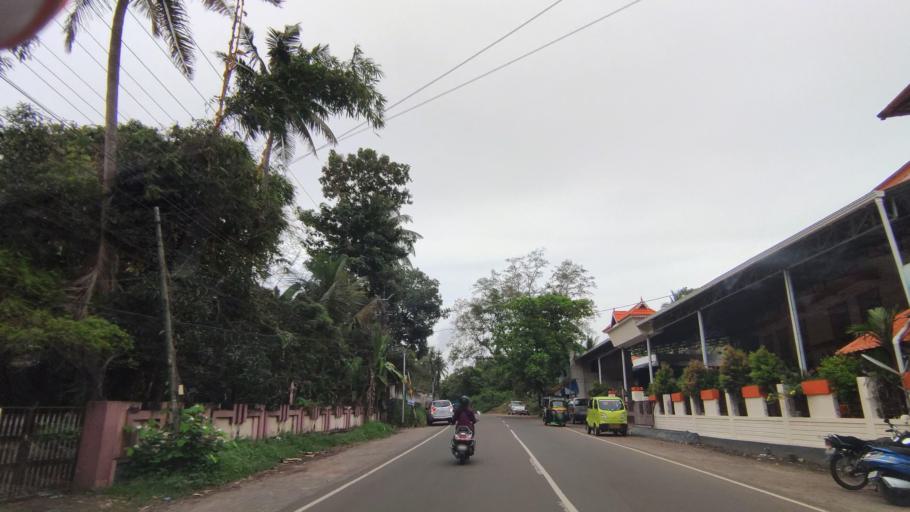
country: IN
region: Kerala
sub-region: Kottayam
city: Kottayam
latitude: 9.6215
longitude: 76.5113
